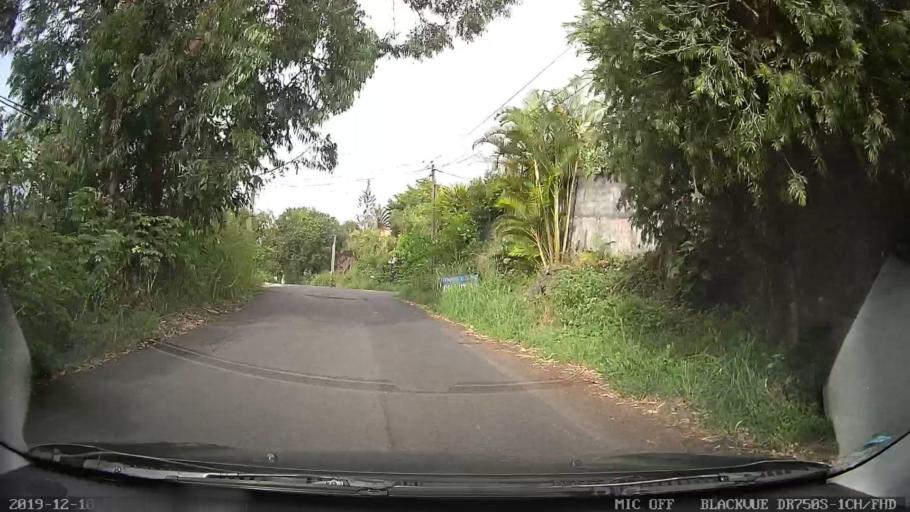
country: RE
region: Reunion
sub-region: Reunion
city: Le Tampon
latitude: -21.2574
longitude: 55.5156
